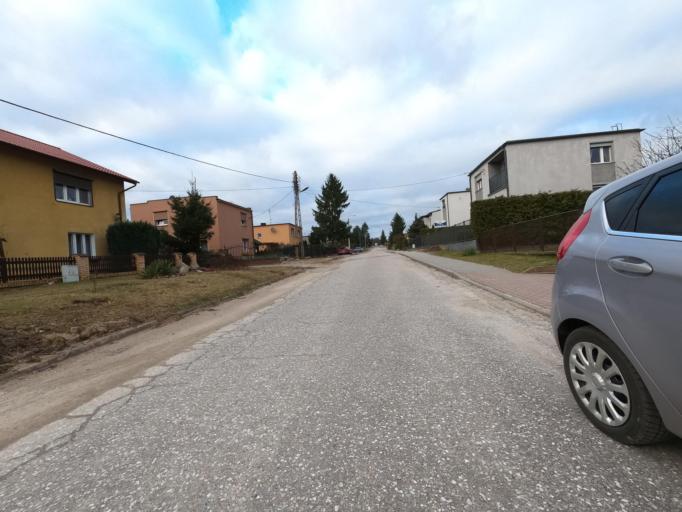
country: PL
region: Greater Poland Voivodeship
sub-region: Powiat pilski
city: Bialosliwie
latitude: 53.1021
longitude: 17.1219
